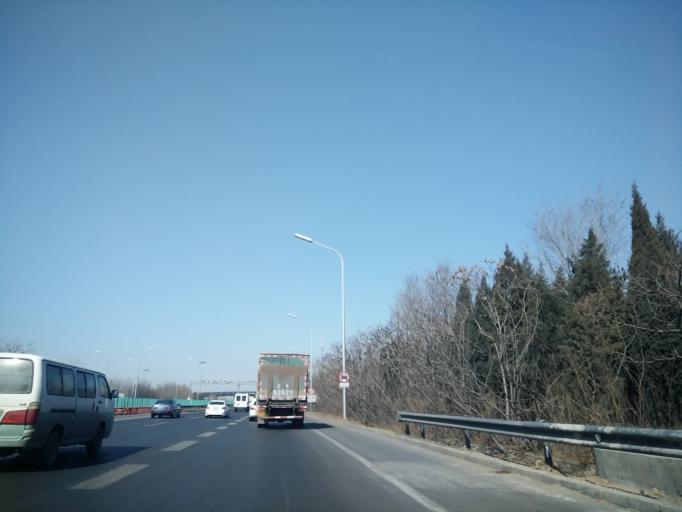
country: CN
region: Beijing
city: Jiugong
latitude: 39.8372
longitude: 116.4764
